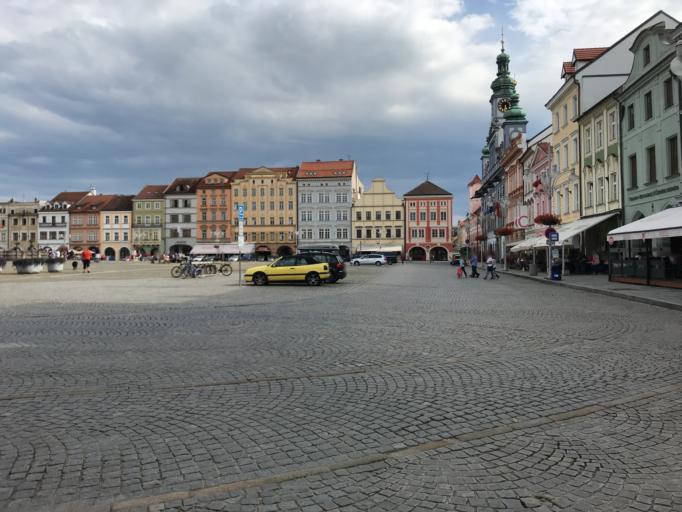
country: CZ
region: Jihocesky
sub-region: Okres Ceske Budejovice
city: Ceske Budejovice
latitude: 48.9752
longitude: 14.4737
